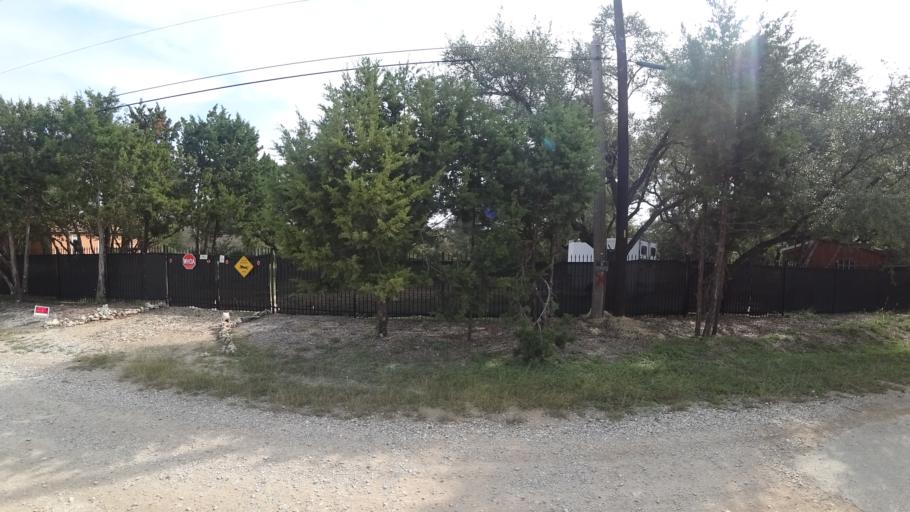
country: US
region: Texas
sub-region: Travis County
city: Hudson Bend
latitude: 30.3854
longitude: -97.9311
